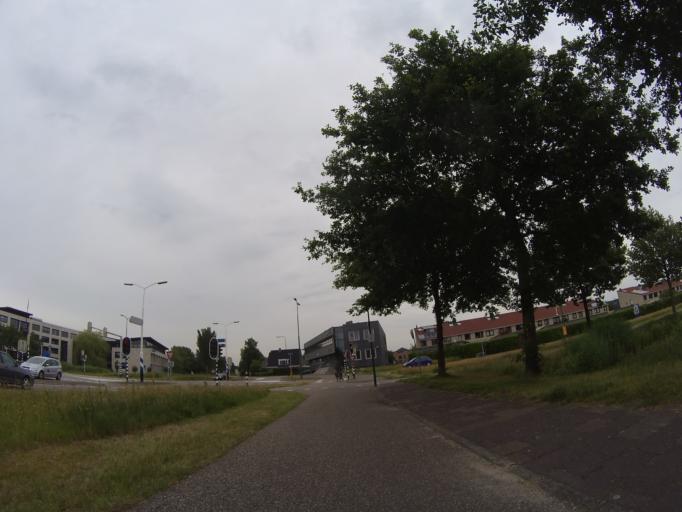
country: NL
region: Utrecht
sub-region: Gemeente Leusden
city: Leusden
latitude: 52.1423
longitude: 5.4249
